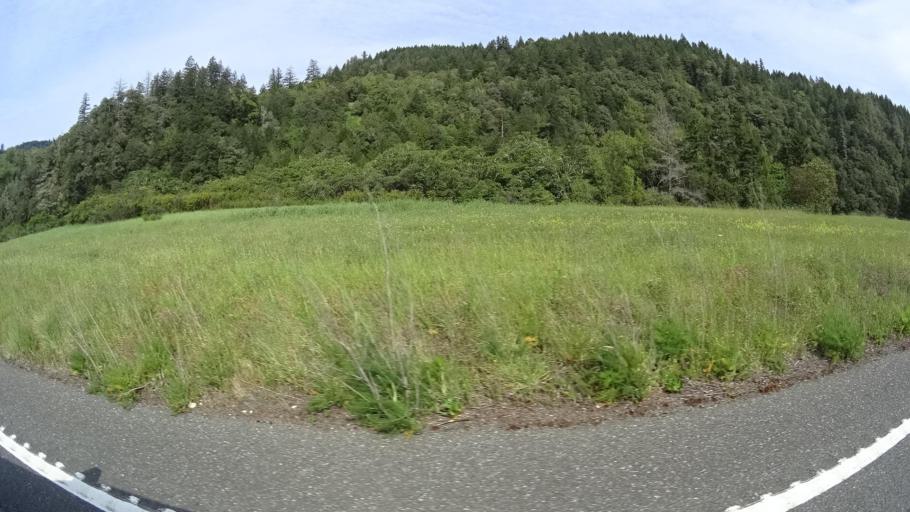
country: US
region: California
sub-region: Humboldt County
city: Redway
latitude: 40.1789
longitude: -123.7795
